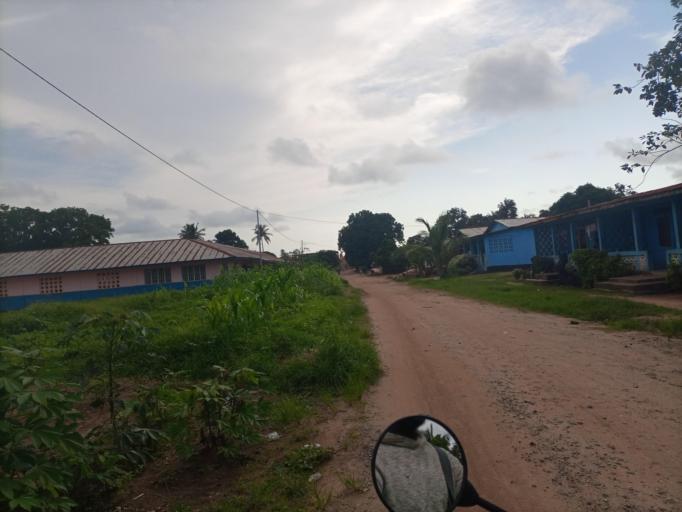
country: SL
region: Northern Province
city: Masoyila
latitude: 8.6109
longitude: -13.1855
